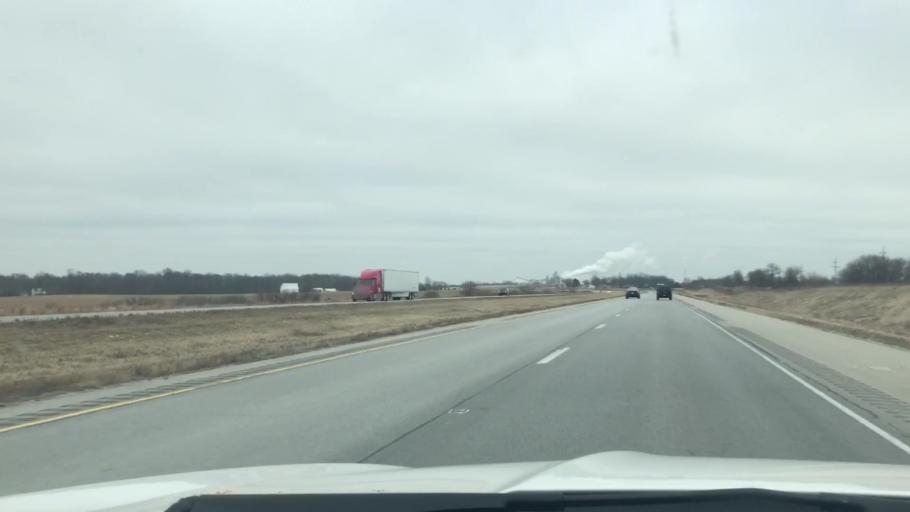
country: US
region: Indiana
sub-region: Cass County
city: Georgetown
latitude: 40.6986
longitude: -86.4661
